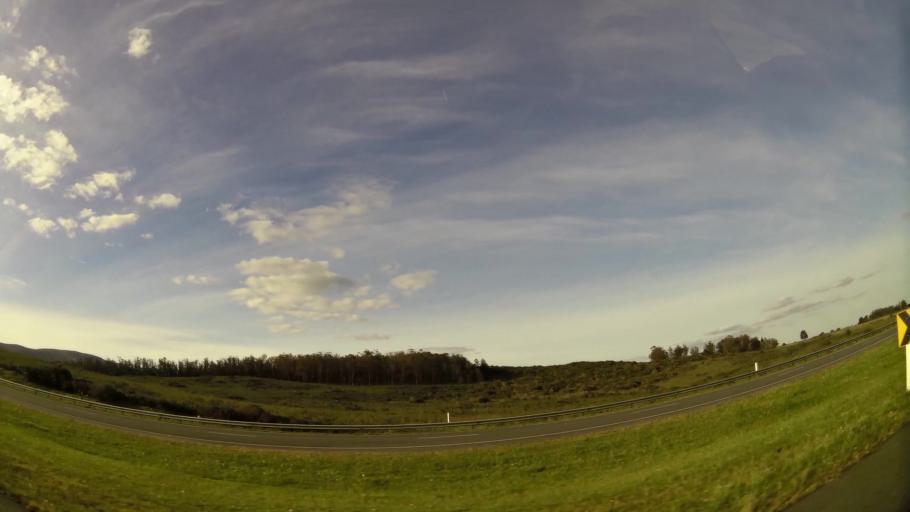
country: UY
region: Maldonado
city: Pan de Azucar
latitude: -34.7855
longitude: -55.2752
